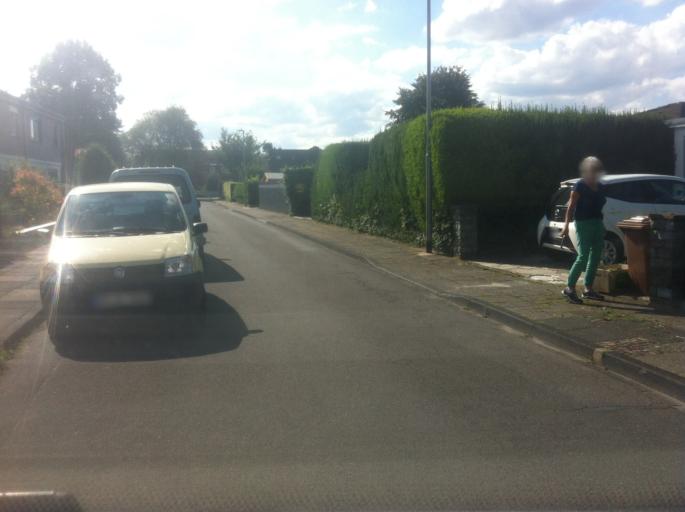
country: DE
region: North Rhine-Westphalia
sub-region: Regierungsbezirk Koln
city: Erftstadt
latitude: 50.8042
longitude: 6.7631
